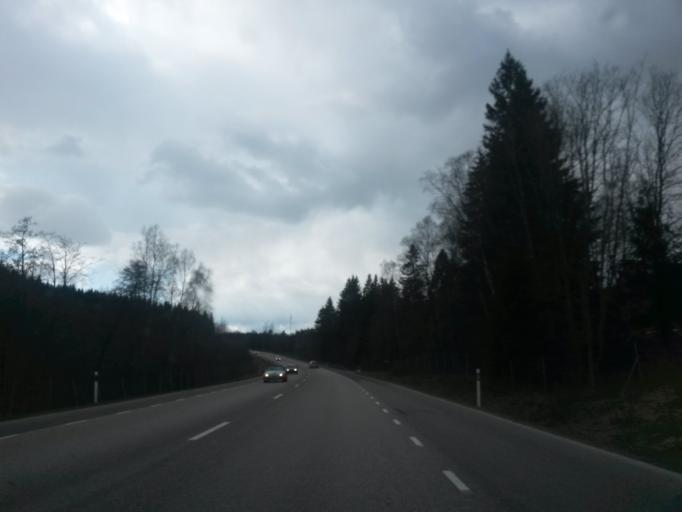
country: SE
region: Vaestra Goetaland
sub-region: Skovde Kommun
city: Skoevde
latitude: 58.3933
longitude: 13.7766
